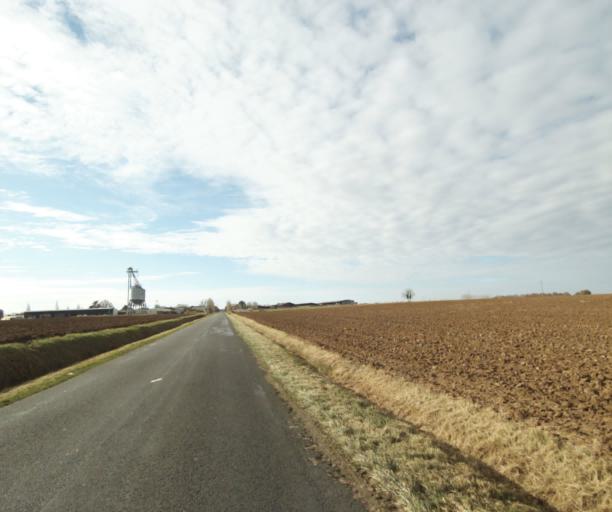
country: FR
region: Poitou-Charentes
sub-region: Departement de la Charente-Maritime
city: Corme-Royal
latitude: 45.7263
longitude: -0.8231
